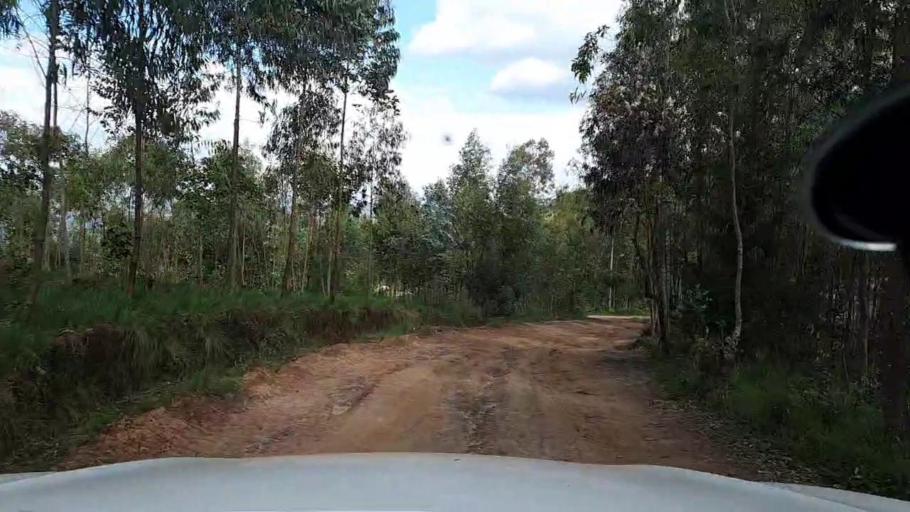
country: RW
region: Kigali
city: Kigali
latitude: -1.7823
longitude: 29.8372
